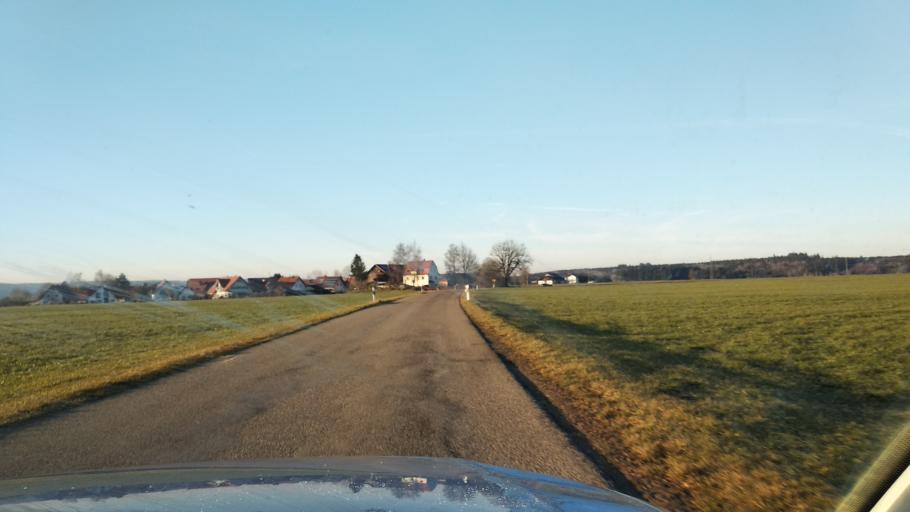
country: DE
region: Bavaria
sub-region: Swabia
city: Lautrach
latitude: 47.9177
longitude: 10.1297
